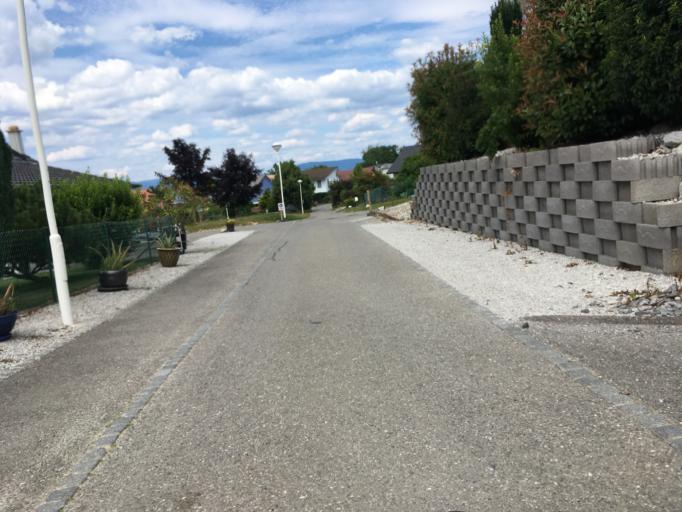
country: CH
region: Fribourg
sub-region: Broye District
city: Estavayer-le-Lac
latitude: 46.8541
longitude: 6.8572
